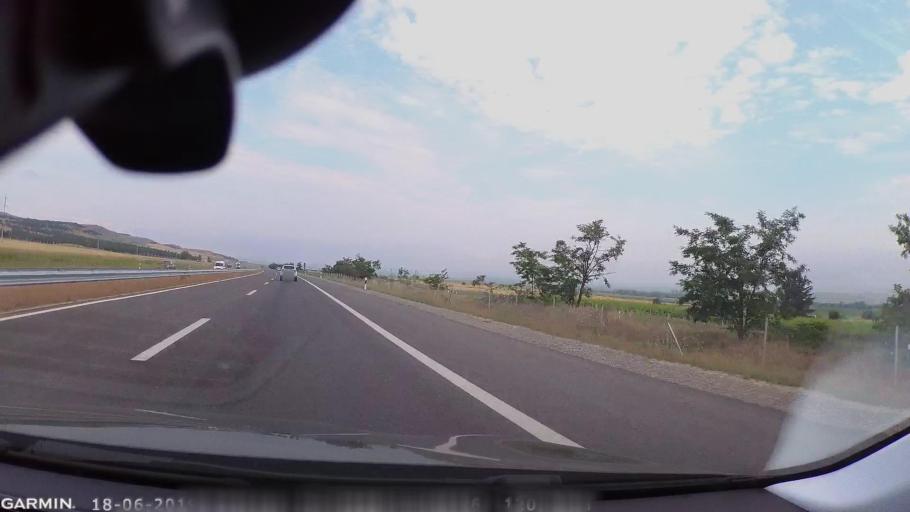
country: MK
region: Stip
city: Shtip
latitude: 41.7952
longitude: 22.0921
